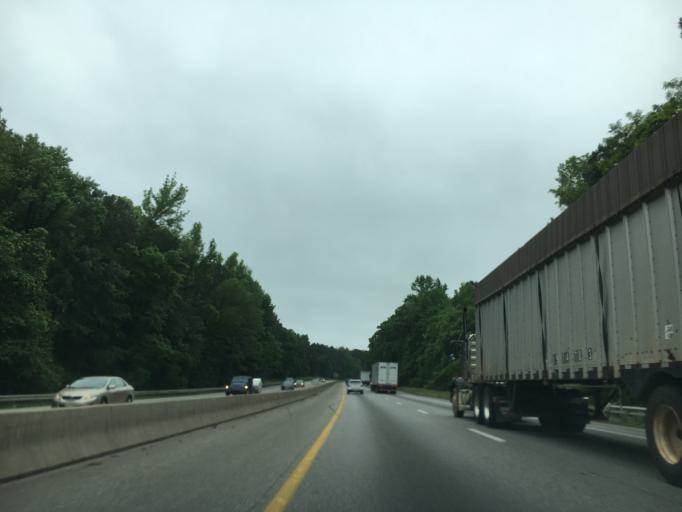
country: US
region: Virginia
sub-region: City of Petersburg
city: Petersburg
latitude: 37.2039
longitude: -77.4134
